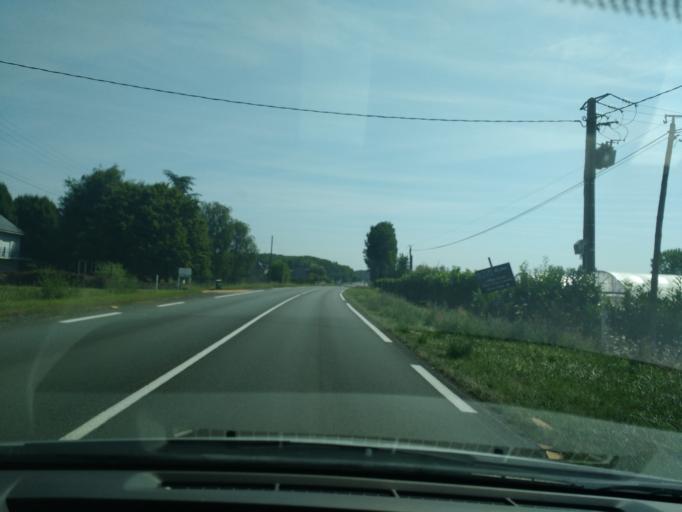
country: FR
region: Pays de la Loire
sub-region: Departement de Maine-et-Loire
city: Baune
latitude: 47.4747
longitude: -0.3240
